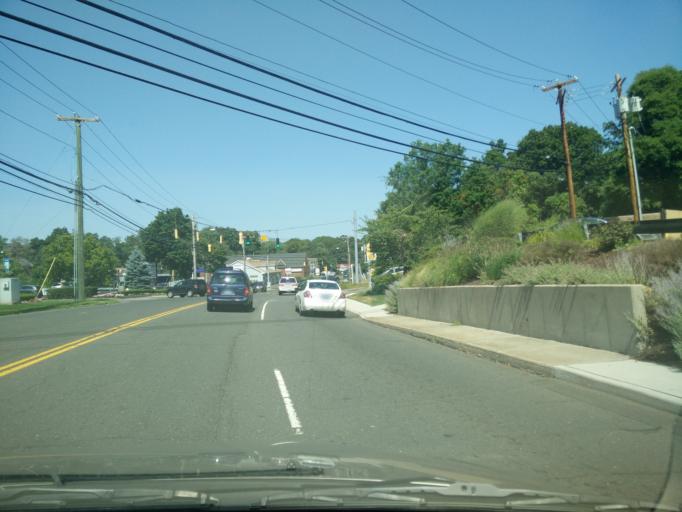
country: US
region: Connecticut
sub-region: Fairfield County
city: Fairfield
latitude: 41.1829
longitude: -73.2547
